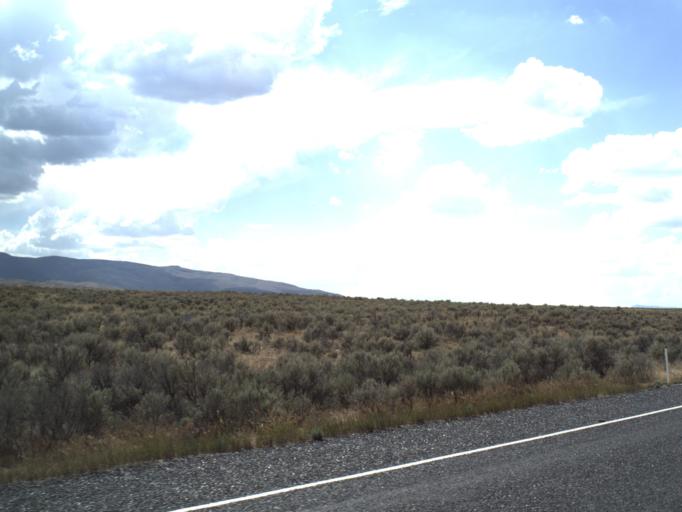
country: US
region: Idaho
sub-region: Minidoka County
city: Rupert
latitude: 41.9846
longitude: -113.1741
